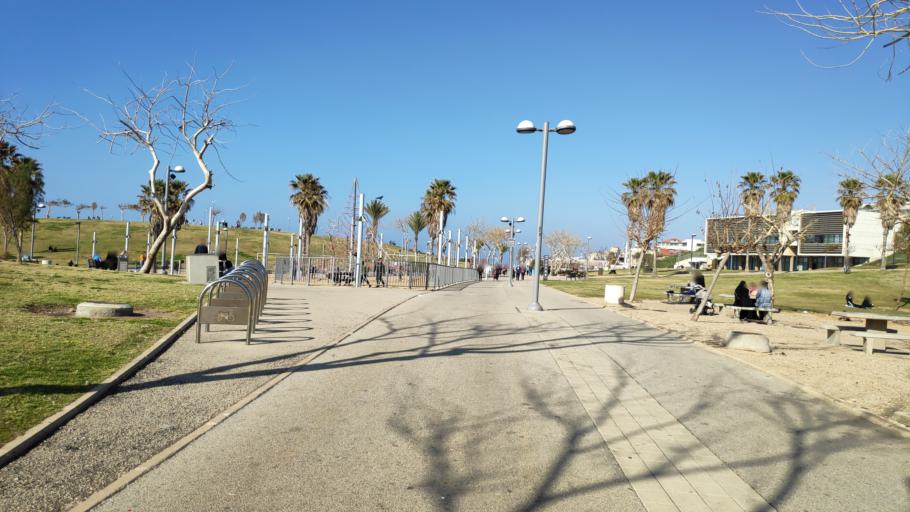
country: IL
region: Tel Aviv
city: Yafo
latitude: 32.0458
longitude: 34.7468
